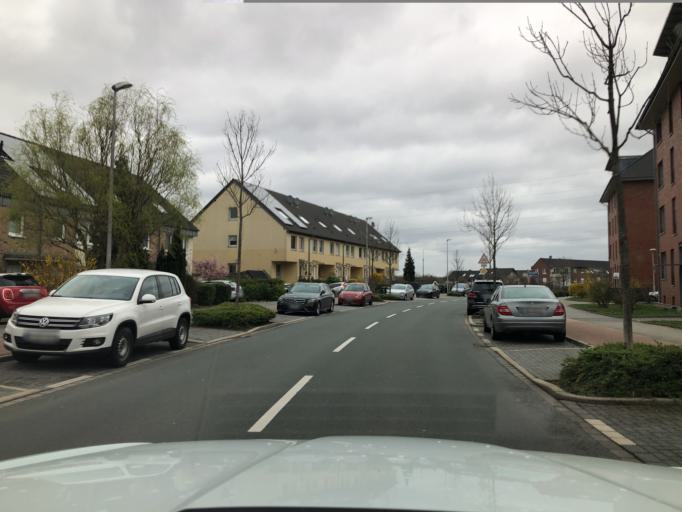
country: DE
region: North Rhine-Westphalia
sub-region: Regierungsbezirk Dusseldorf
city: Muelheim (Ruhr)
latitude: 51.3979
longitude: 6.8638
